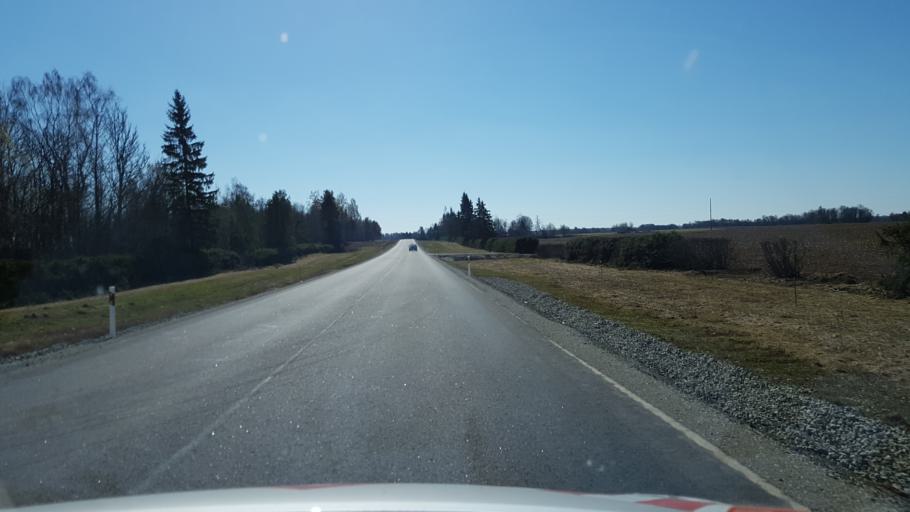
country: EE
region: Laeaene-Virumaa
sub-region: Vinni vald
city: Vinni
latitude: 59.0855
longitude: 26.6264
